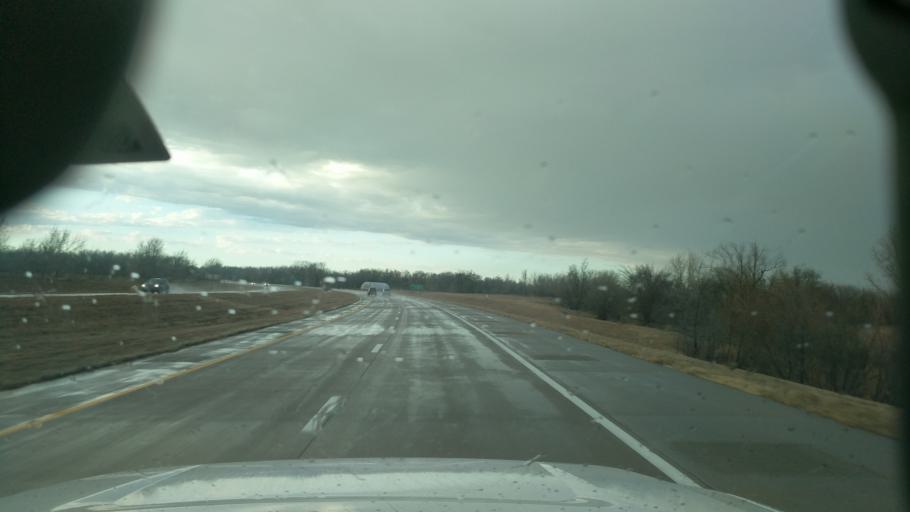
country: US
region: Kansas
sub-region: Harvey County
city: North Newton
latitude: 38.0767
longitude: -97.3308
